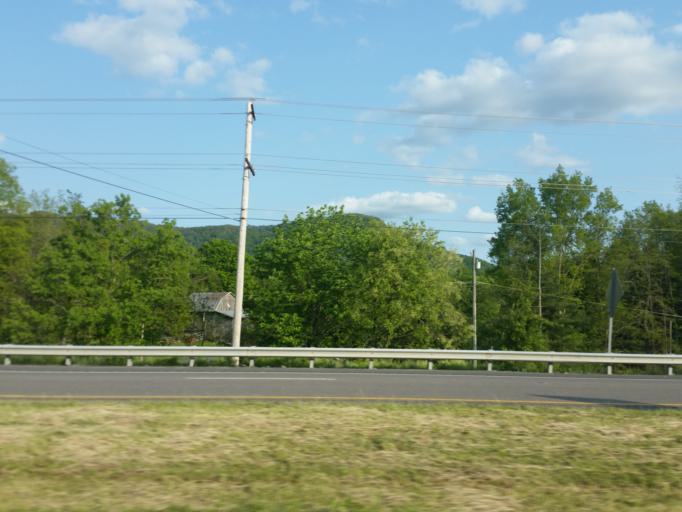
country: US
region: Virginia
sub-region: Tazewell County
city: Claypool Hill
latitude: 37.0599
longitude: -81.7591
